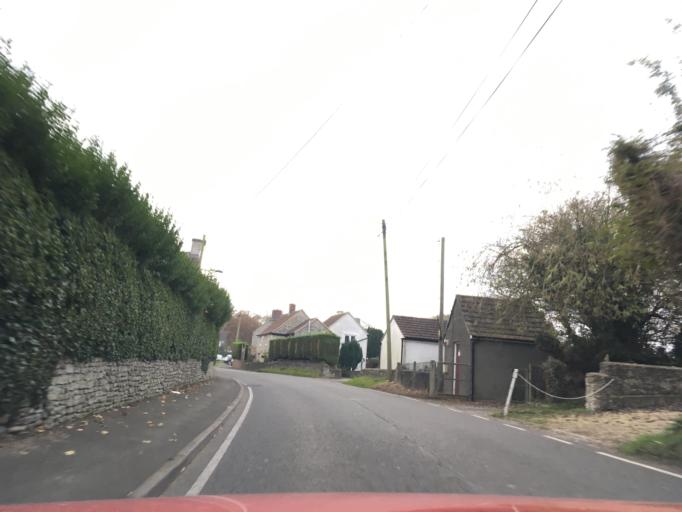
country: GB
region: England
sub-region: South Gloucestershire
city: Pucklechurch
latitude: 51.4899
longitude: -2.4334
